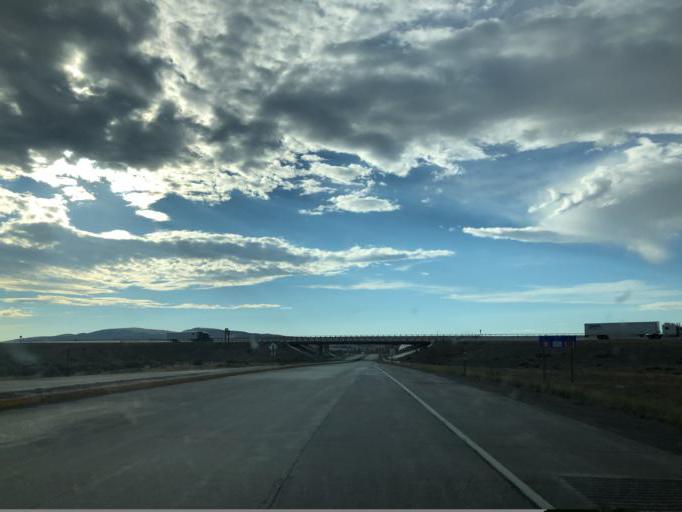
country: US
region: Wyoming
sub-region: Carbon County
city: Rawlins
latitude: 41.7878
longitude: -107.1982
